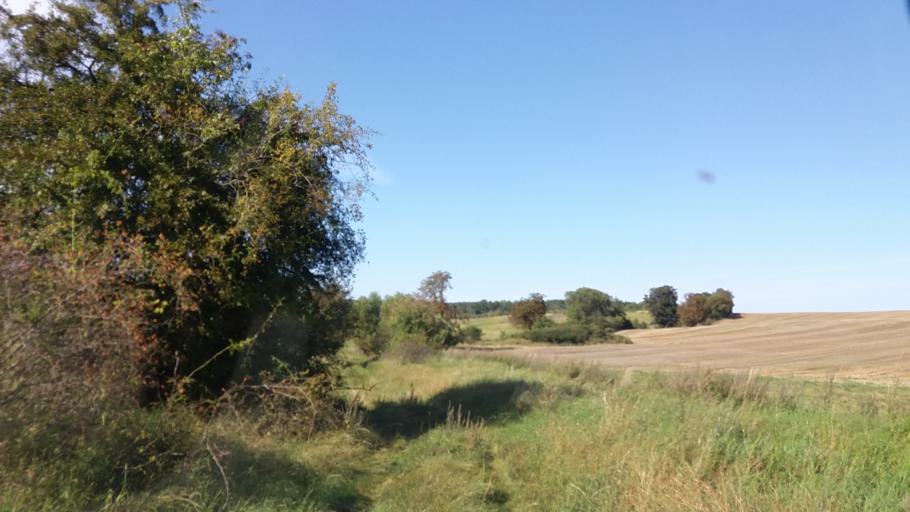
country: PL
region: West Pomeranian Voivodeship
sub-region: Powiat choszczenski
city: Krzecin
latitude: 53.1264
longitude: 15.5016
